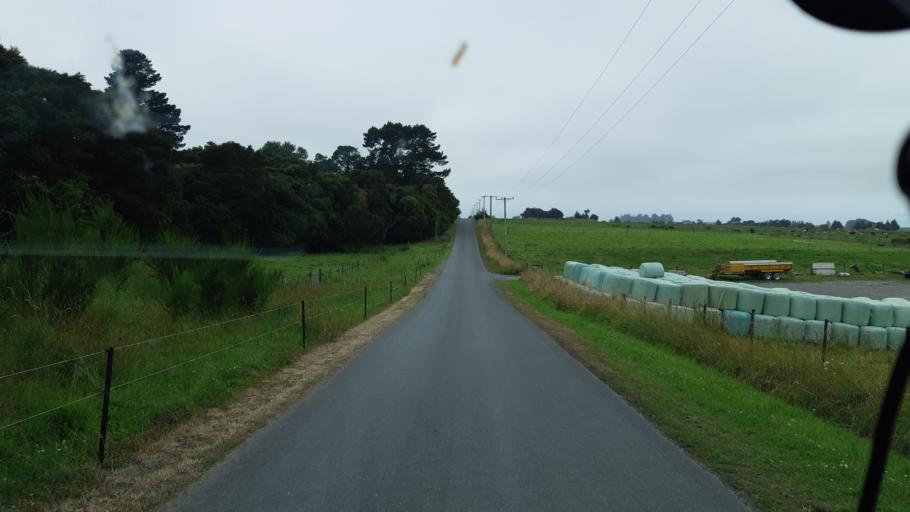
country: NZ
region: Canterbury
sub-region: Kaikoura District
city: Kaikoura
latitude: -42.3116
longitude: 173.6890
